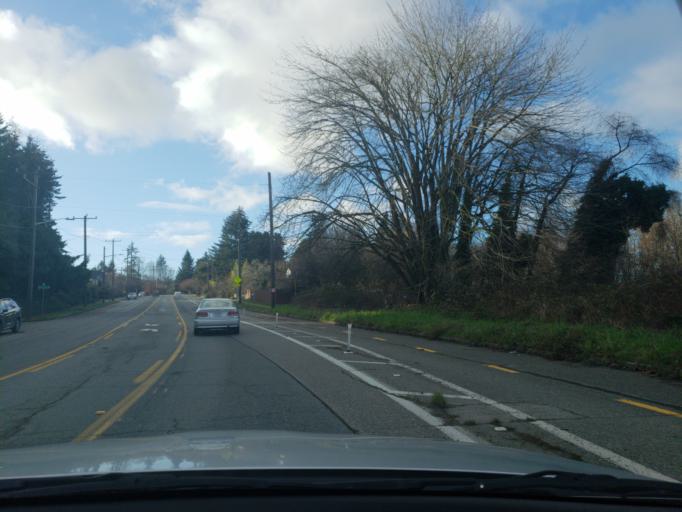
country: US
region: Washington
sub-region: King County
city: Seattle
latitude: 47.6613
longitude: -122.3943
